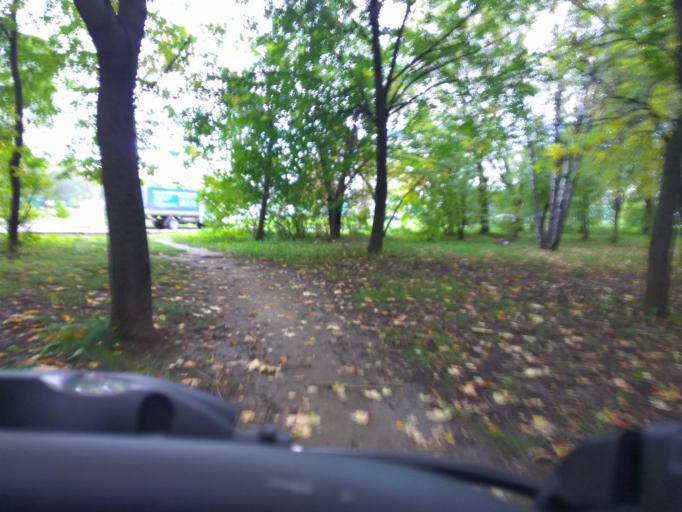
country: RU
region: Moscow
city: Kozeyevo
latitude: 55.8746
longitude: 37.6149
